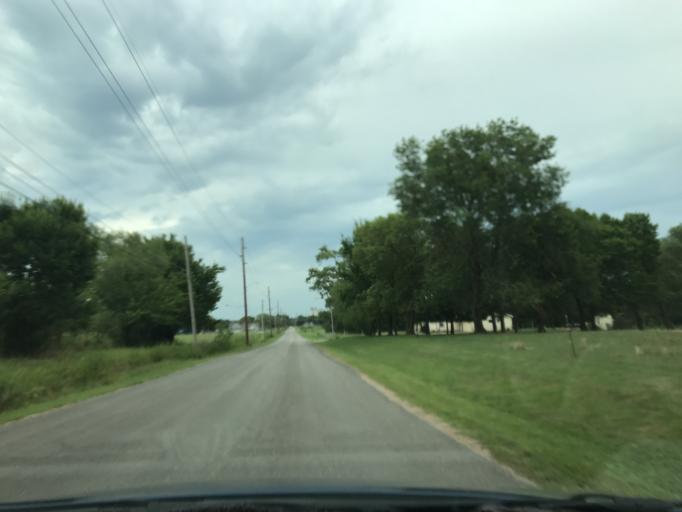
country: US
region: Nebraska
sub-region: Gage County
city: Beatrice
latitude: 40.2629
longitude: -96.7744
